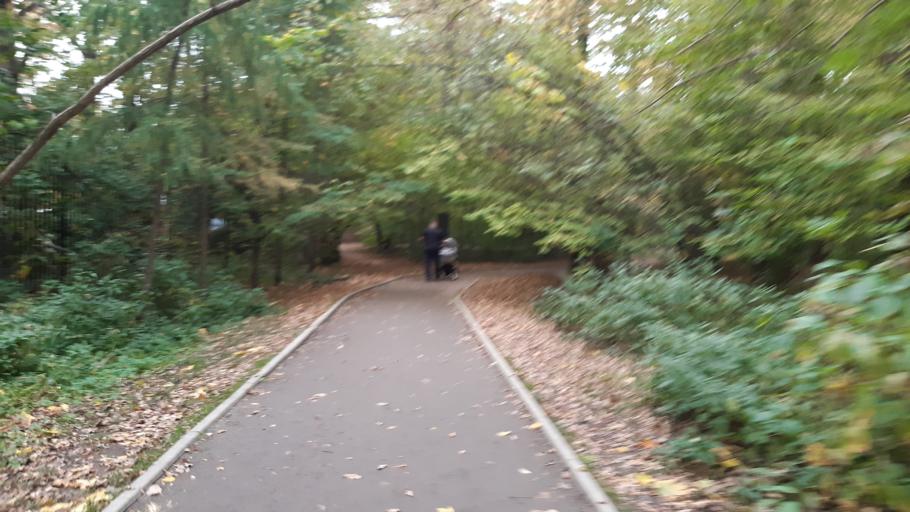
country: RU
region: Moscow
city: Vagonoremont
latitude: 55.9019
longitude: 37.5624
